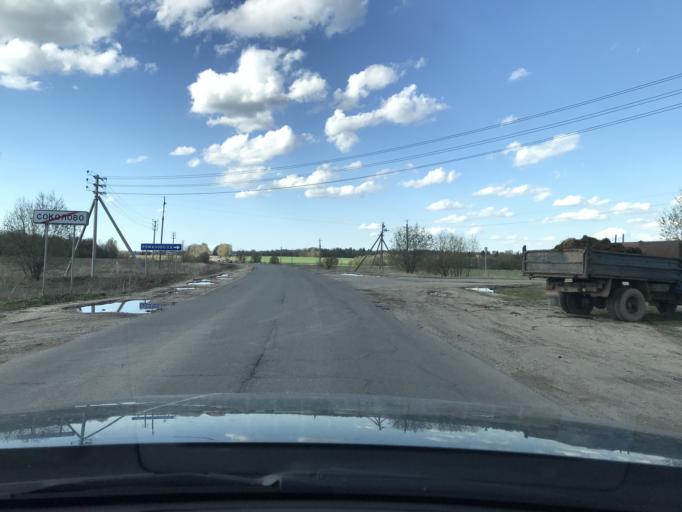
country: RU
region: Vladimir
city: Strunino
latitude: 56.3977
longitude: 38.5860
